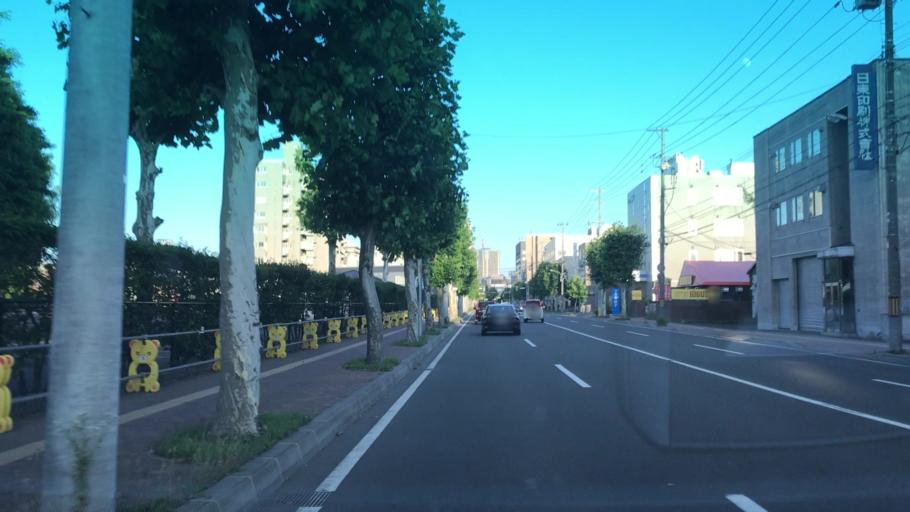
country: JP
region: Hokkaido
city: Sapporo
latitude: 43.0741
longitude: 141.3260
